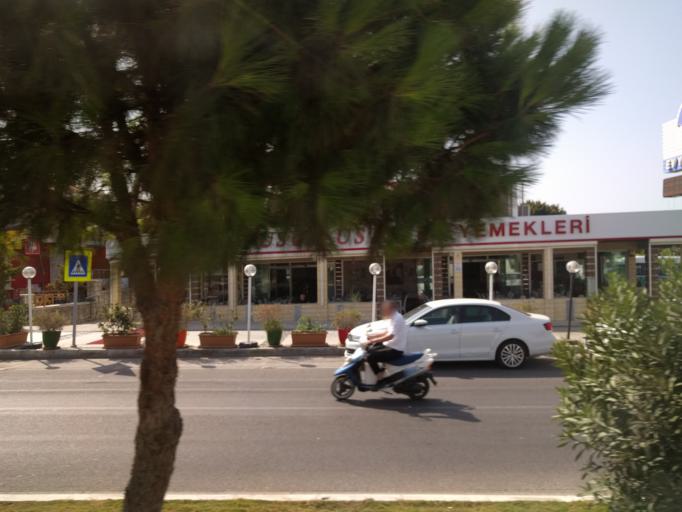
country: TR
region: Izmir
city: Alacati
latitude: 38.2870
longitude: 26.3716
